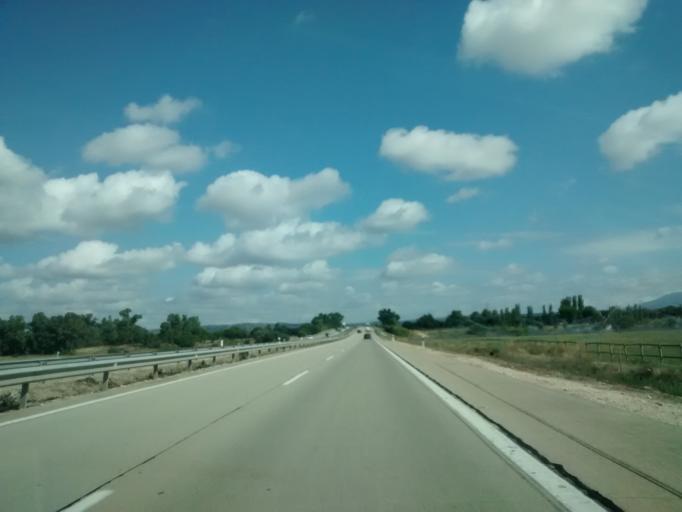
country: ES
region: Castille-La Mancha
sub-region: Province of Toledo
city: Talavera de la Reina
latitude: 39.9915
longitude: -4.7600
